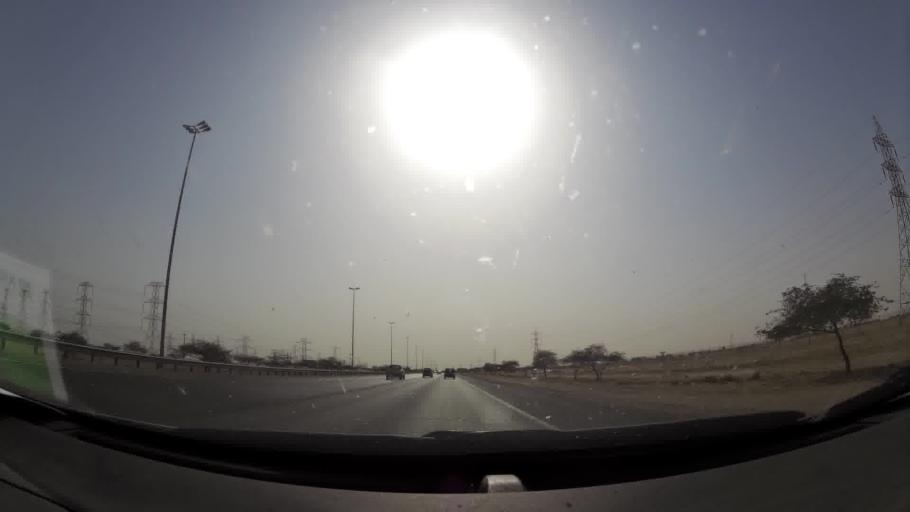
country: KW
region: Al Ahmadi
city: Al Ahmadi
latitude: 28.9799
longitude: 48.1084
